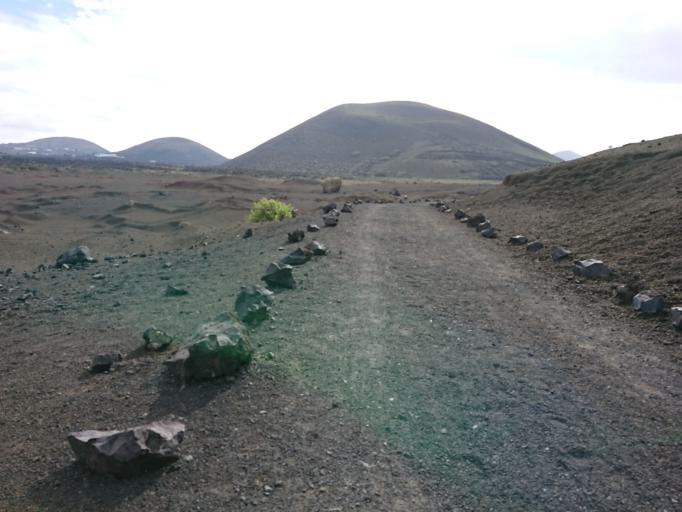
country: ES
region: Canary Islands
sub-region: Provincia de Las Palmas
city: Tias
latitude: 29.0052
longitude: -13.6759
